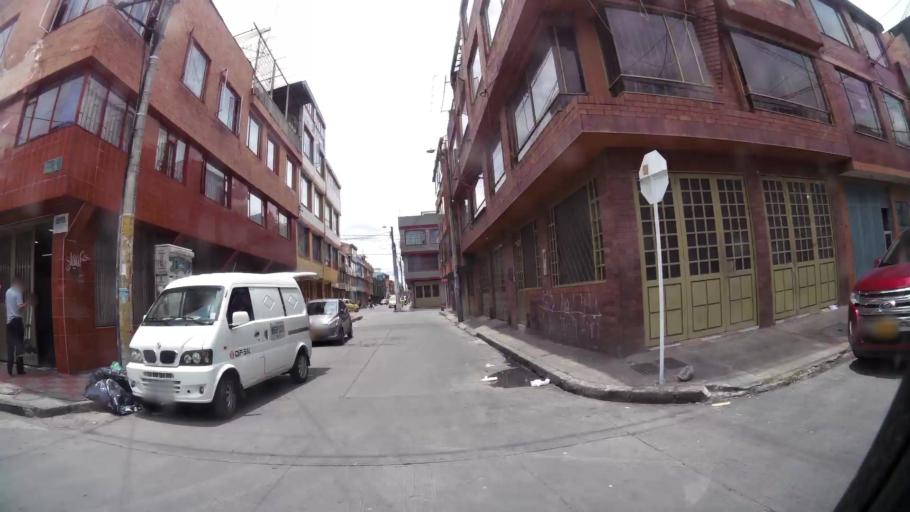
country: CO
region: Cundinamarca
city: Funza
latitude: 4.7070
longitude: -74.1259
